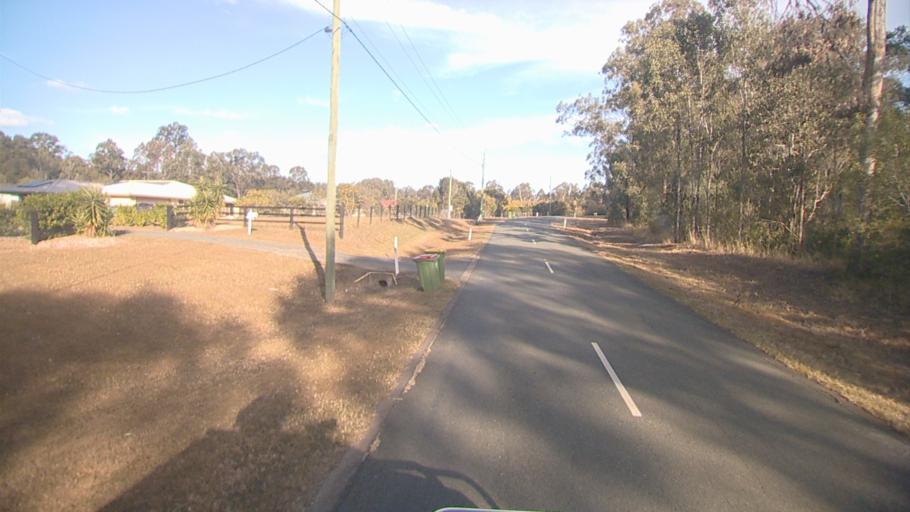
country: AU
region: Queensland
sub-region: Logan
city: Cedar Vale
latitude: -27.8802
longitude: 153.0105
